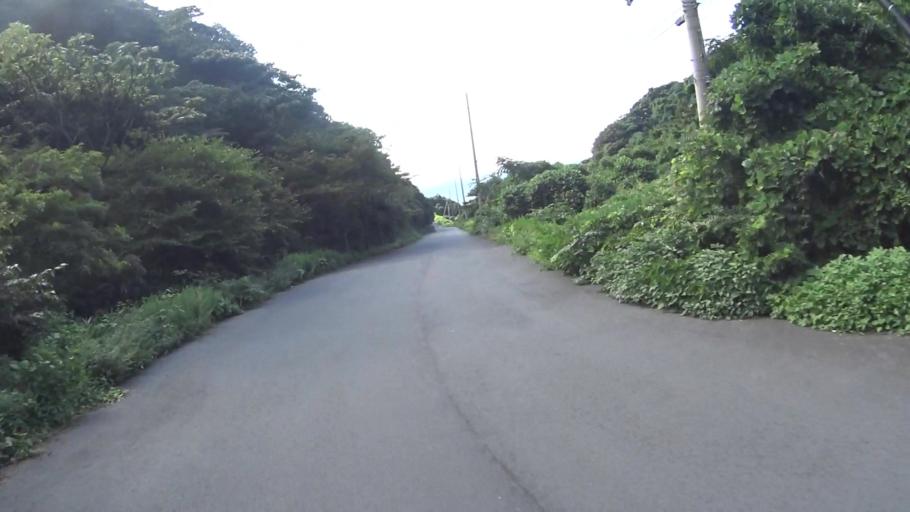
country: JP
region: Kyoto
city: Miyazu
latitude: 35.7696
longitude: 135.2249
